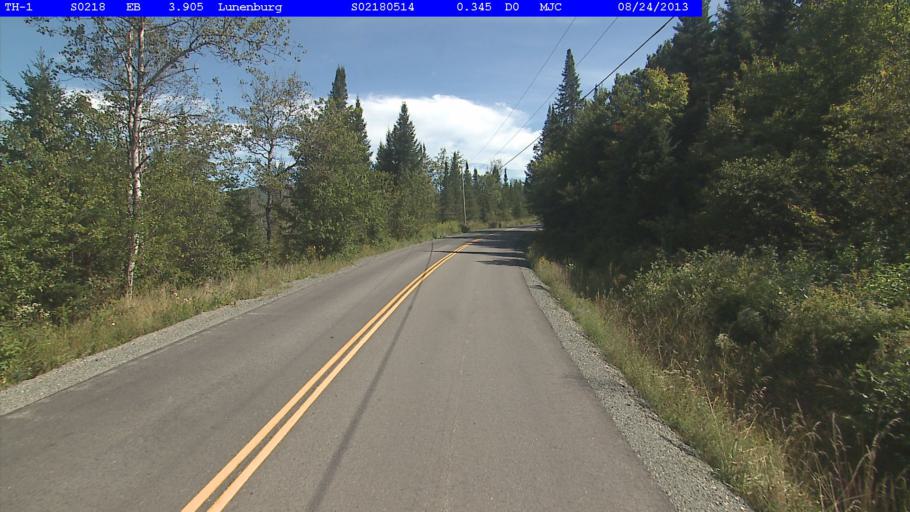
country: US
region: New Hampshire
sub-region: Grafton County
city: Littleton
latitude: 44.4183
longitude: -71.7415
